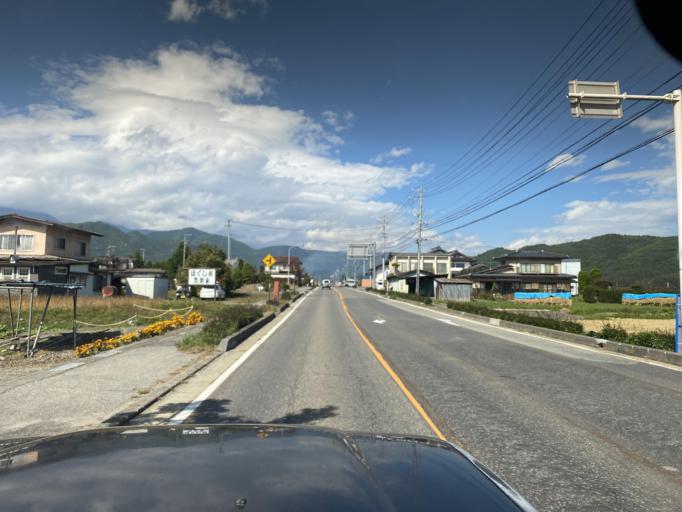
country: JP
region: Nagano
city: Omachi
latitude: 36.5218
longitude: 137.8525
